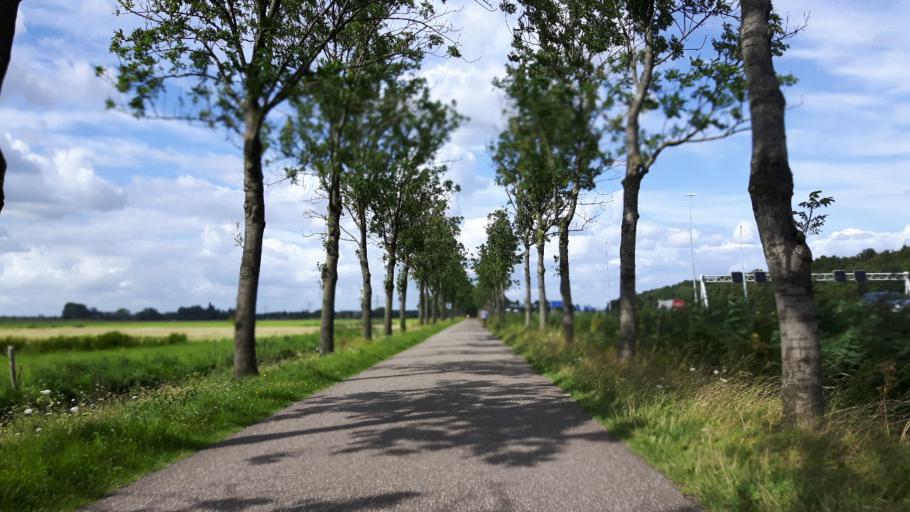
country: NL
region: Utrecht
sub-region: Gemeente Nieuwegein
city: Nieuwegein
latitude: 52.0479
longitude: 5.0640
